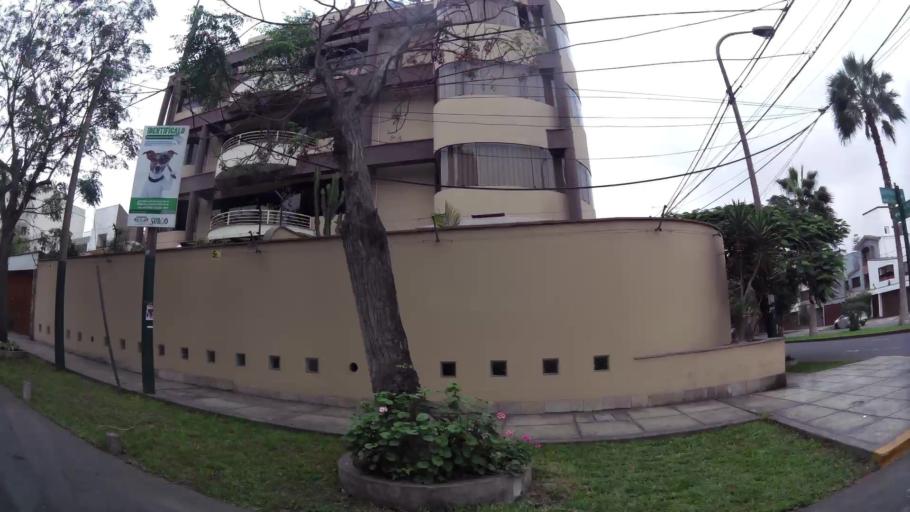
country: PE
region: Lima
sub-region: Lima
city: Surco
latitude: -12.1194
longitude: -76.9833
